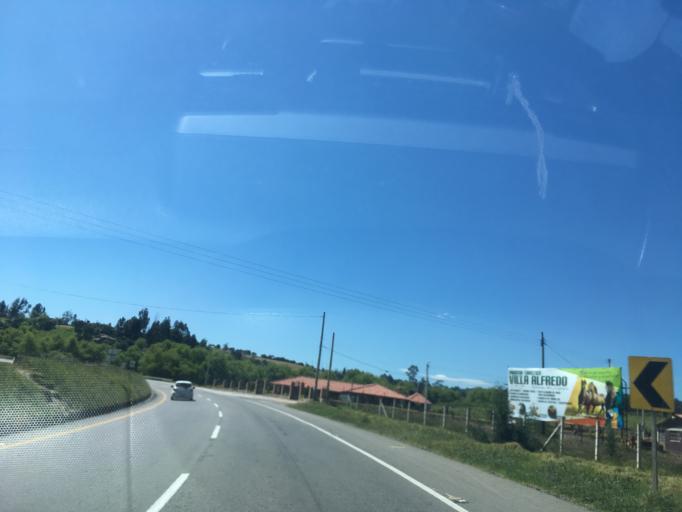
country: CO
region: Boyaca
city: Tuta
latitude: 5.7093
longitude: -73.2444
